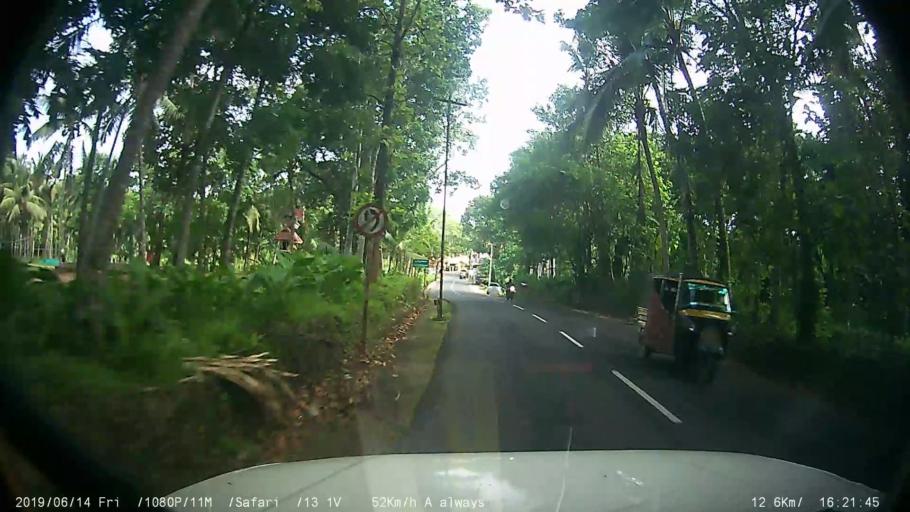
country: IN
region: Kerala
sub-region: Kottayam
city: Palackattumala
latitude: 9.7730
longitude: 76.6112
